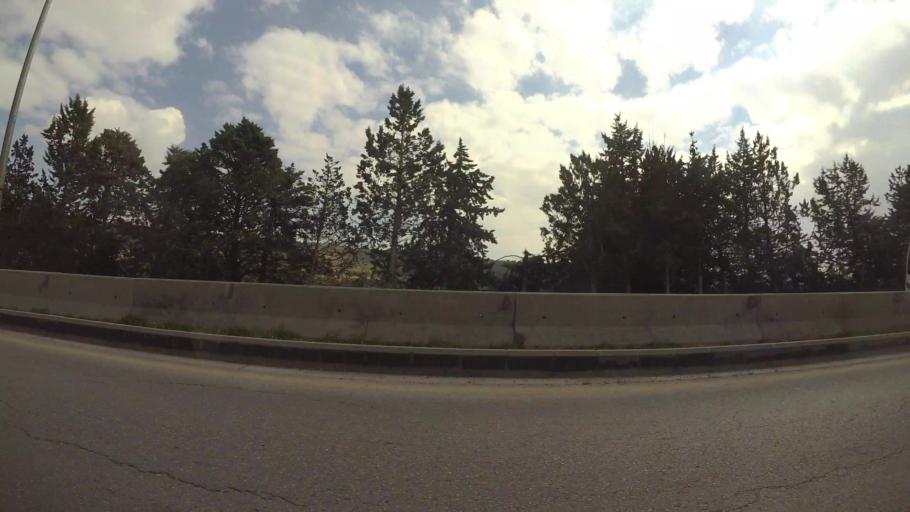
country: JO
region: Amman
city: Al Jubayhah
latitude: 32.0283
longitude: 35.8158
